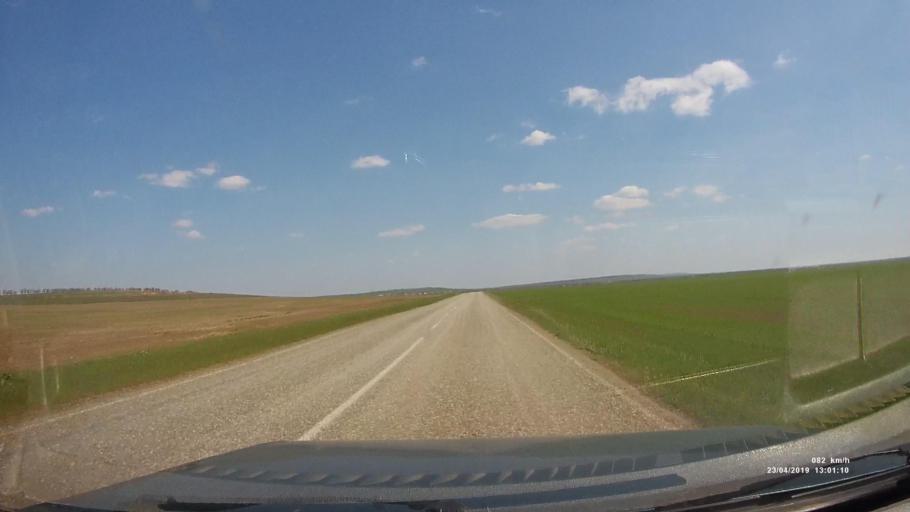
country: RU
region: Kalmykiya
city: Yashalta
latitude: 46.6039
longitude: 42.6475
